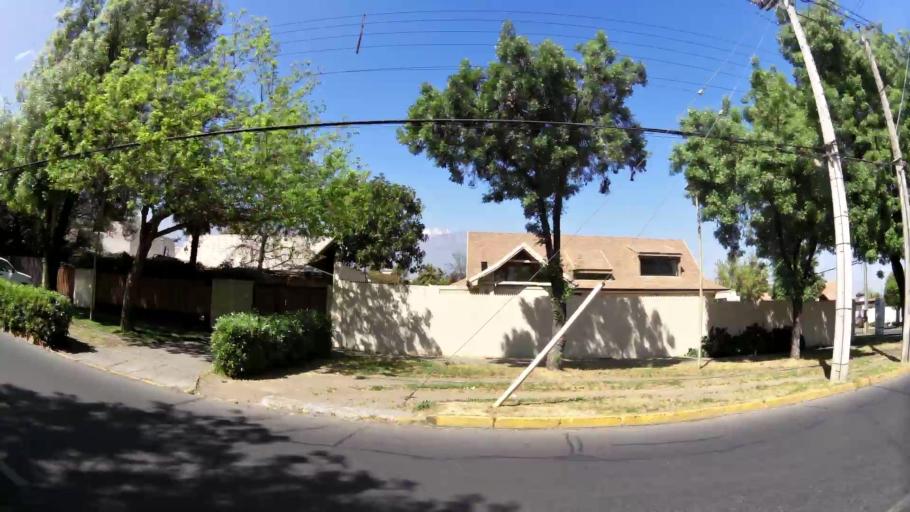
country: CL
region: Santiago Metropolitan
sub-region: Provincia de Santiago
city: Villa Presidente Frei, Nunoa, Santiago, Chile
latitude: -33.4113
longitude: -70.5458
